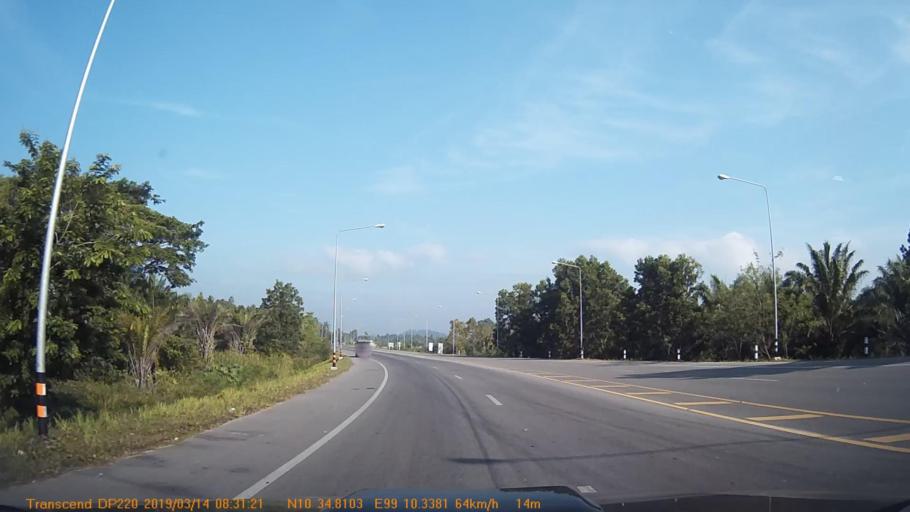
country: TH
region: Chumphon
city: Tha Sae
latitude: 10.5804
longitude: 99.1722
